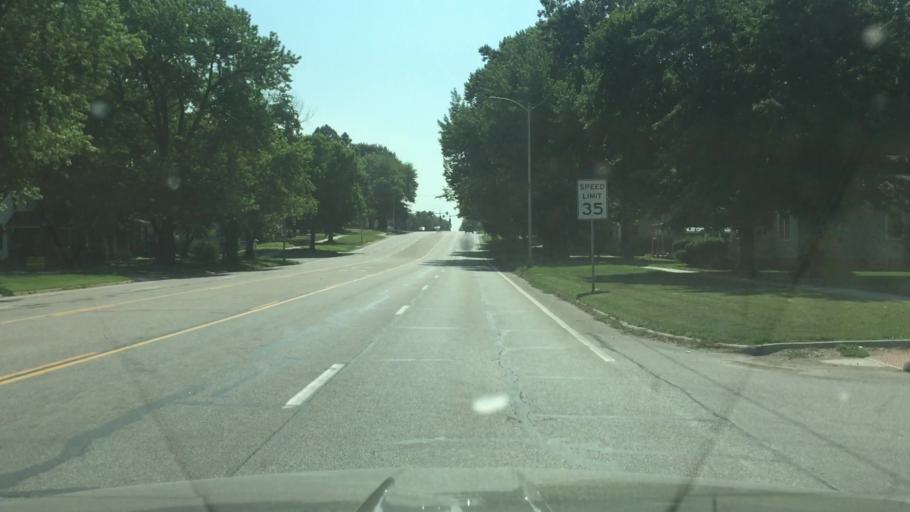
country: US
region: Missouri
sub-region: Pettis County
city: Sedalia
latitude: 38.7037
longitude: -93.2169
